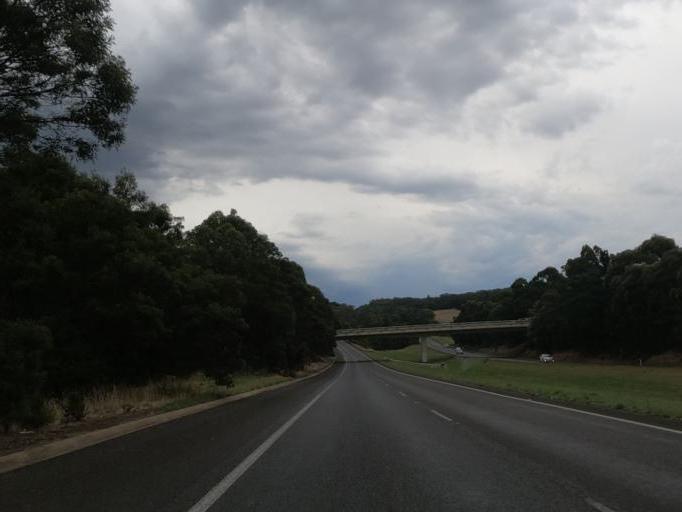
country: AU
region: Victoria
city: Brown Hill
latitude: -37.5449
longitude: 143.8921
